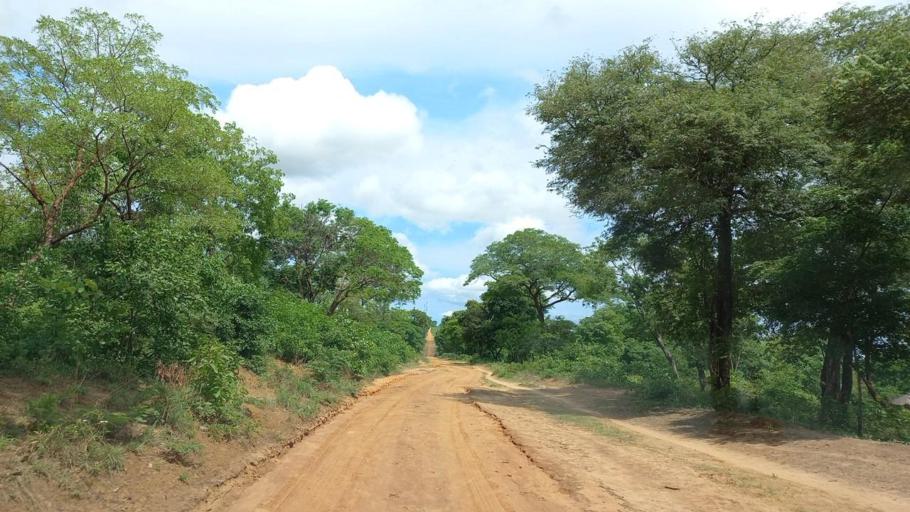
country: ZM
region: North-Western
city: Kabompo
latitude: -13.5441
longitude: 24.1025
